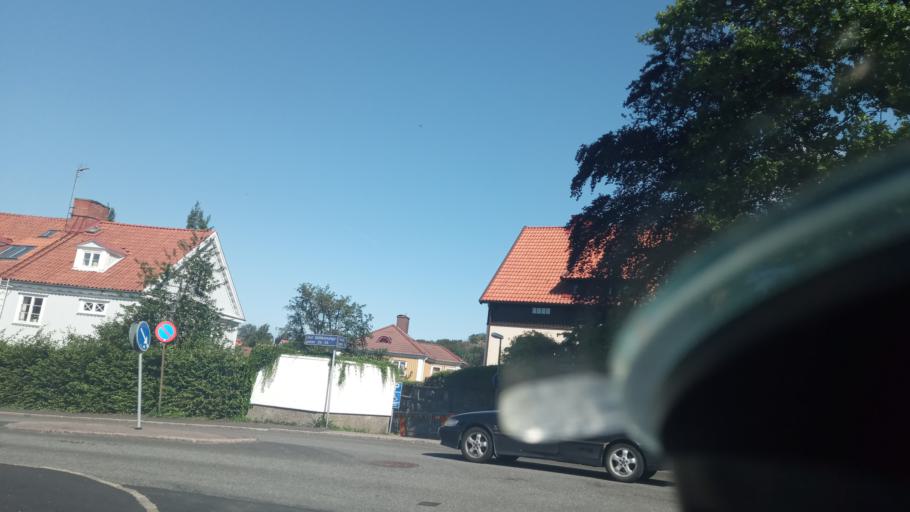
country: SE
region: Vaestra Goetaland
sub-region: Goteborg
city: Goeteborg
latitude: 57.6968
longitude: 12.0032
